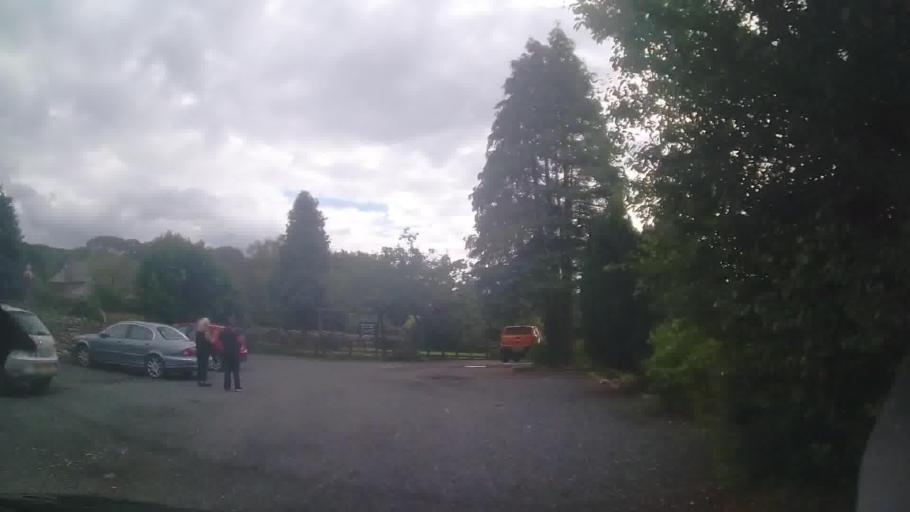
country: GB
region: England
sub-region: Cumbria
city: Millom
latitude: 54.3983
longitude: -3.2703
